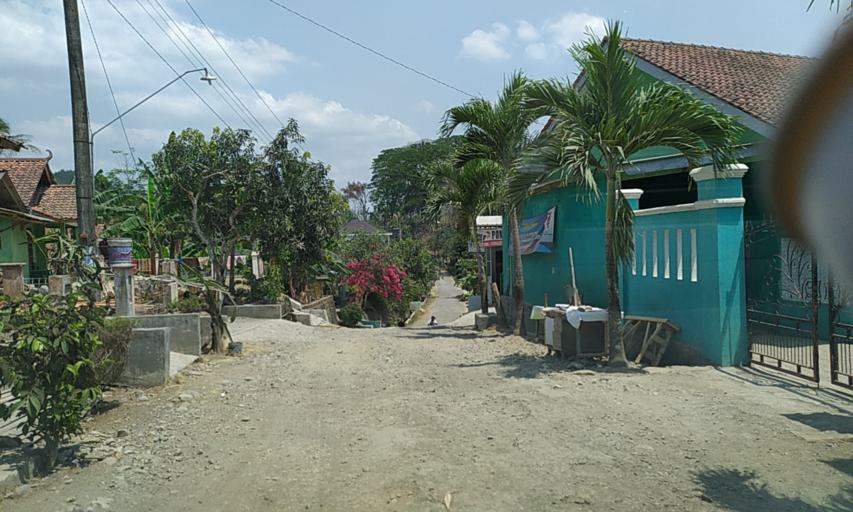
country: ID
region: Central Java
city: Cidadap
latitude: -7.4031
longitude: 108.8612
